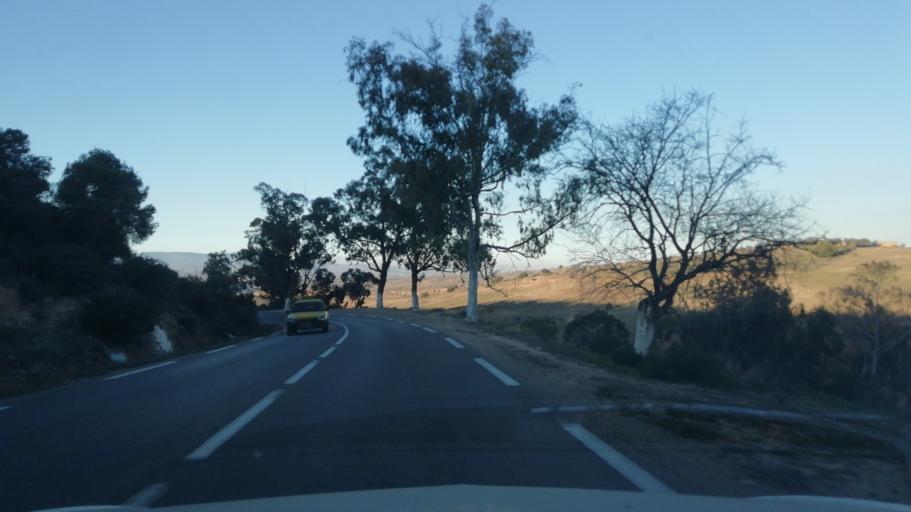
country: DZ
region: Tlemcen
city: Beni Mester
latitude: 34.8198
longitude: -1.6362
